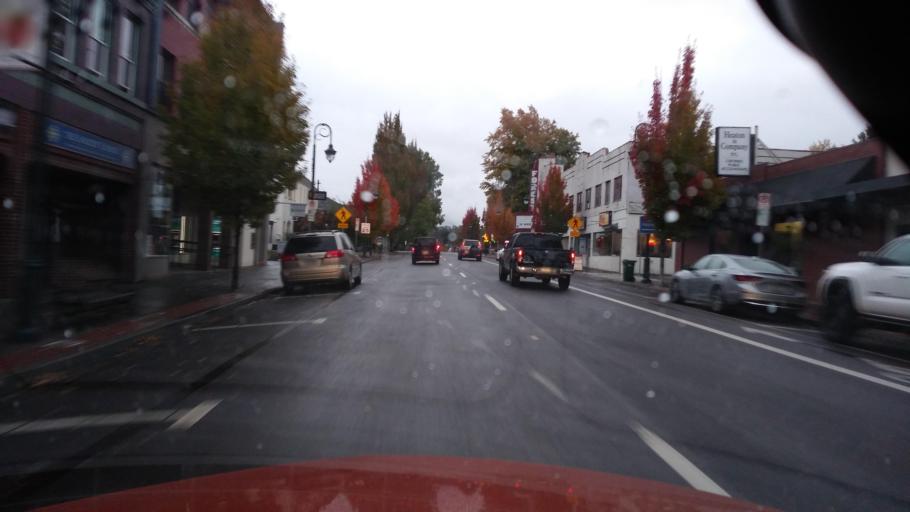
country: US
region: Oregon
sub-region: Washington County
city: Forest Grove
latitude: 45.5197
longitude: -123.1123
